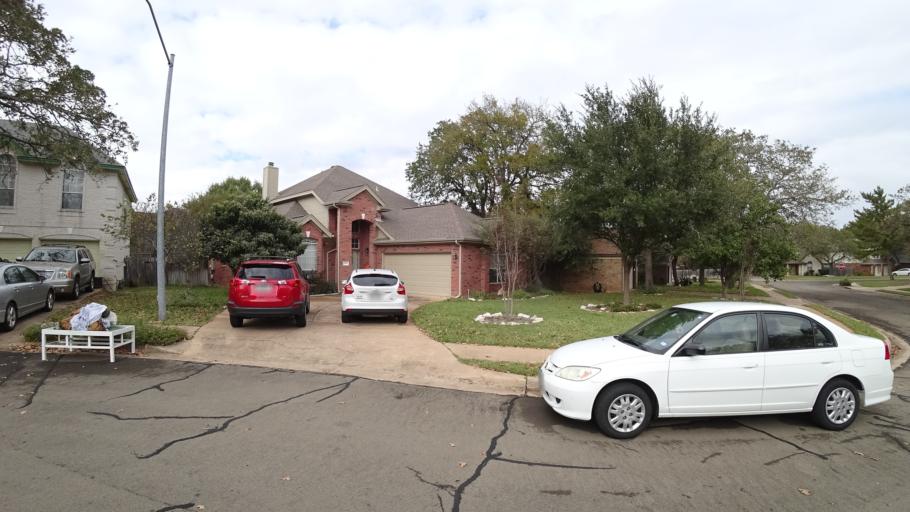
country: US
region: Texas
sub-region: Williamson County
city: Brushy Creek
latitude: 30.5154
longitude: -97.7166
